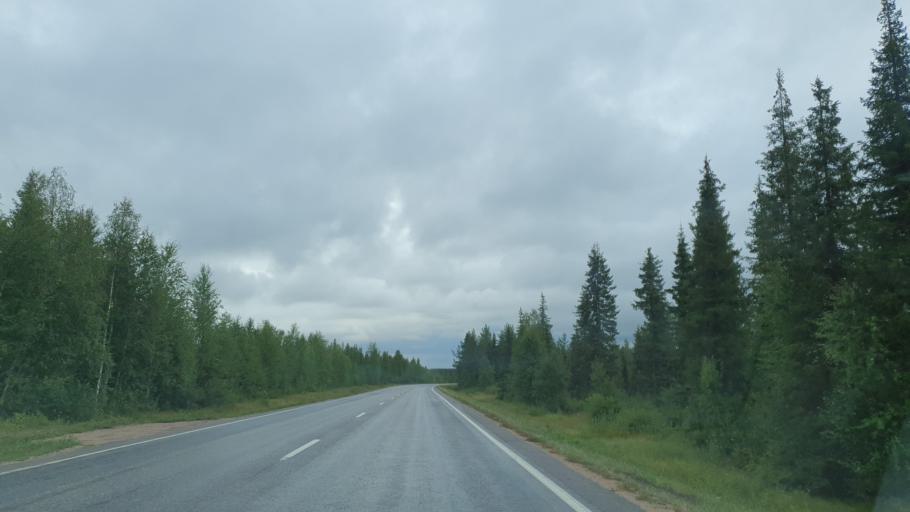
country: FI
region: Lapland
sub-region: Tunturi-Lappi
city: Kolari
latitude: 67.2254
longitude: 23.8977
